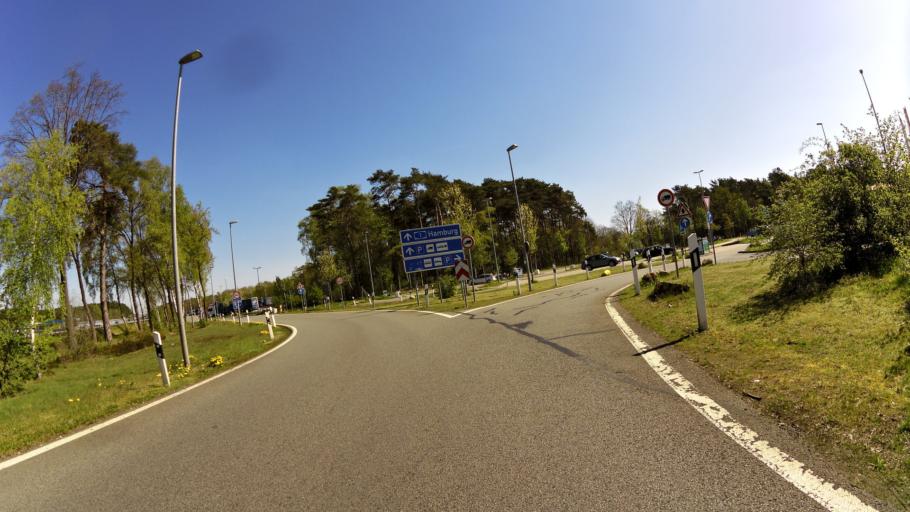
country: DE
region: Lower Saxony
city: Ottersberg
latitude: 53.0884
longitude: 9.1767
